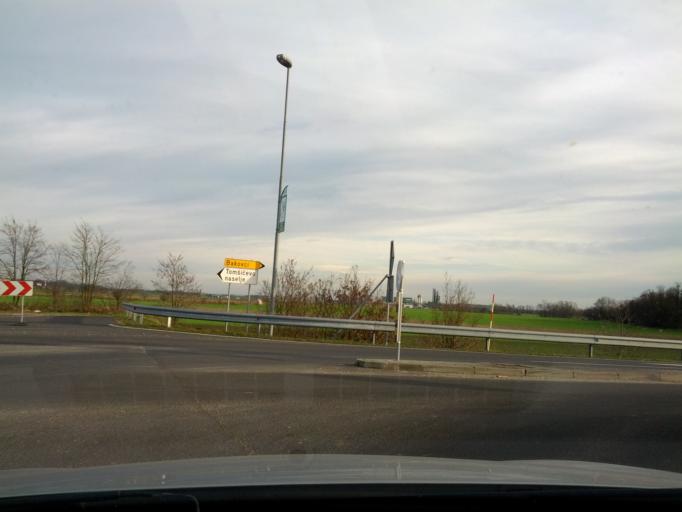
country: SI
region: Murska Sobota
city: Krog
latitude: 46.6477
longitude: 16.1535
